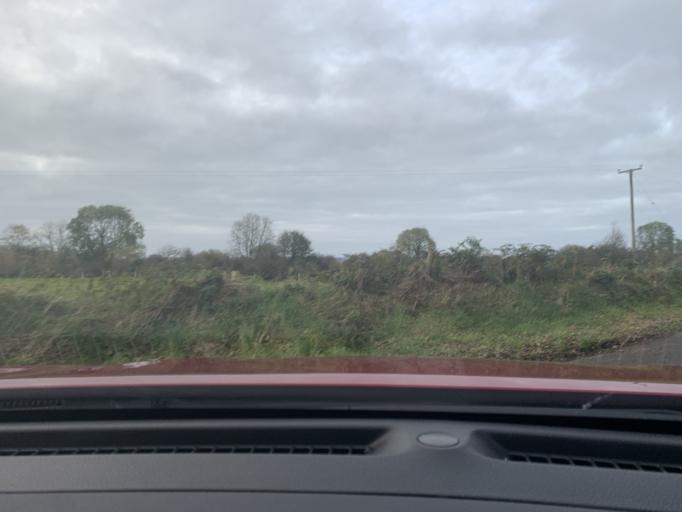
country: IE
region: Connaught
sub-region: Sligo
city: Tobercurry
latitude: 54.0298
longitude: -8.7003
